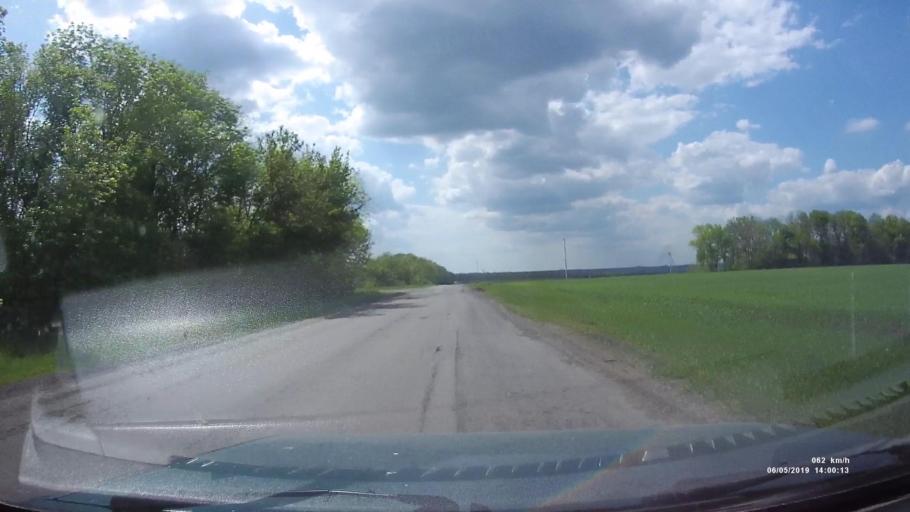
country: RU
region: Rostov
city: Shakhty
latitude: 47.6853
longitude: 40.3917
